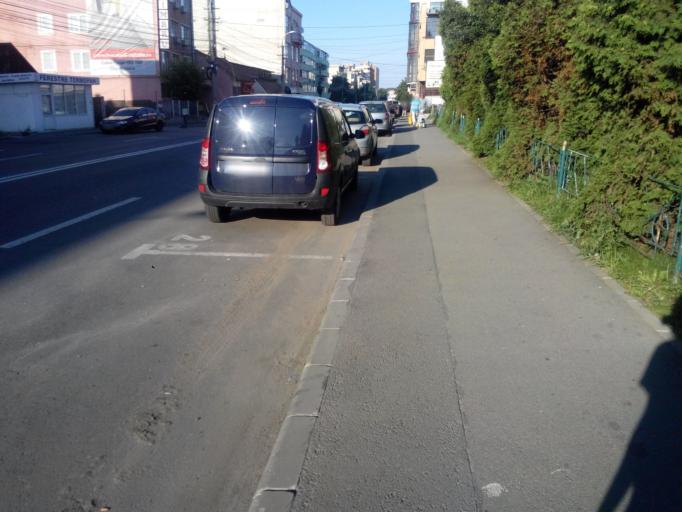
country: RO
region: Cluj
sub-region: Municipiul Cluj-Napoca
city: Cluj-Napoca
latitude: 46.7810
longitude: 23.6072
